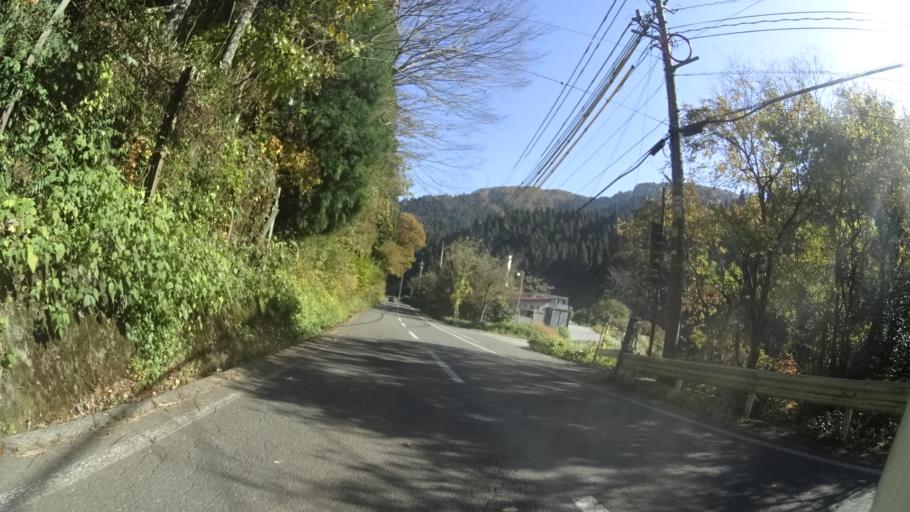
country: JP
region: Fukui
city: Ono
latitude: 35.9327
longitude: 136.3585
